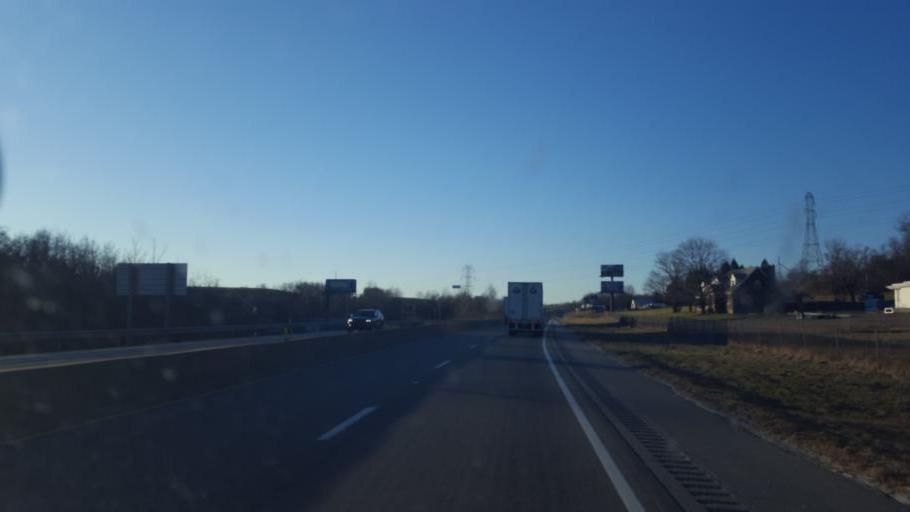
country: US
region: Pennsylvania
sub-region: Washington County
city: Bentleyville
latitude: 40.1453
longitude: -80.0275
